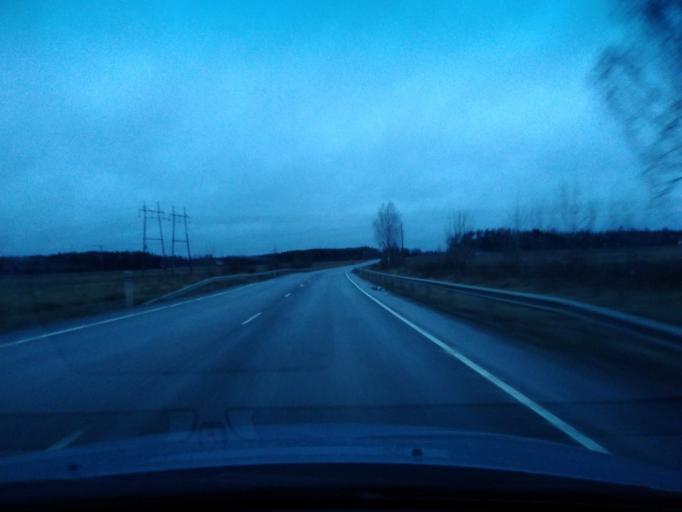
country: FI
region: Uusimaa
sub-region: Porvoo
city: Porvoo
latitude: 60.3959
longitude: 25.6012
